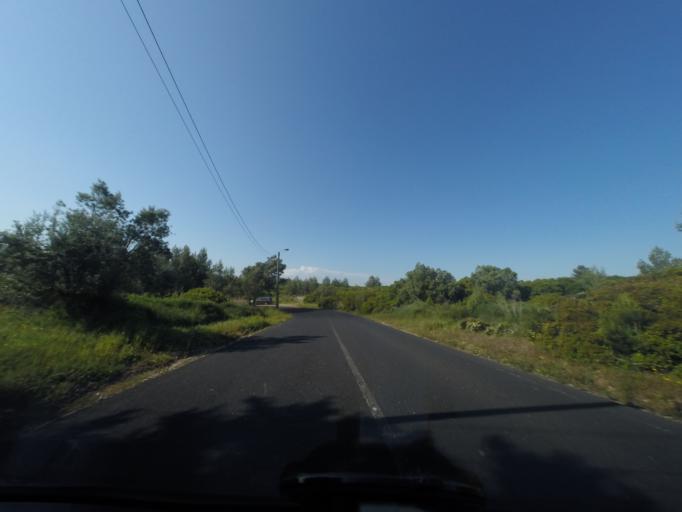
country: PT
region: Lisbon
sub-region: Cascais
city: Alcabideche
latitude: 38.7419
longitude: -9.4285
